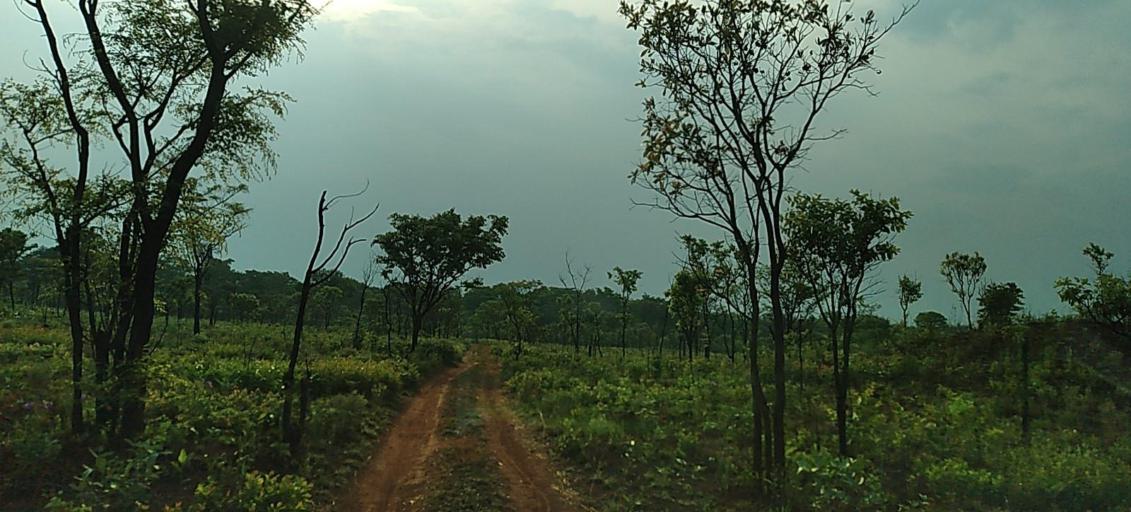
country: ZM
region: North-Western
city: Solwezi
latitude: -12.0419
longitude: 26.0433
